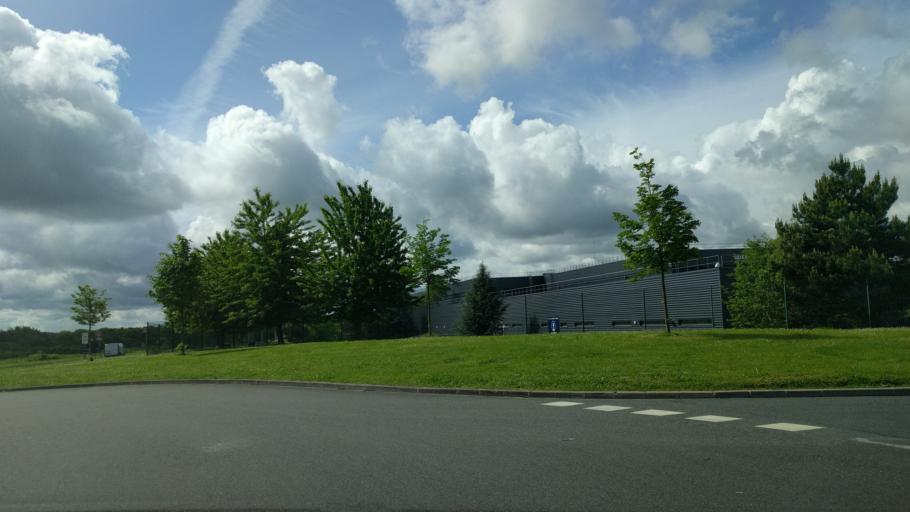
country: FR
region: Ile-de-France
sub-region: Departement de Seine-et-Marne
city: Savigny-le-Temple
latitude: 48.5794
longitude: 2.5942
